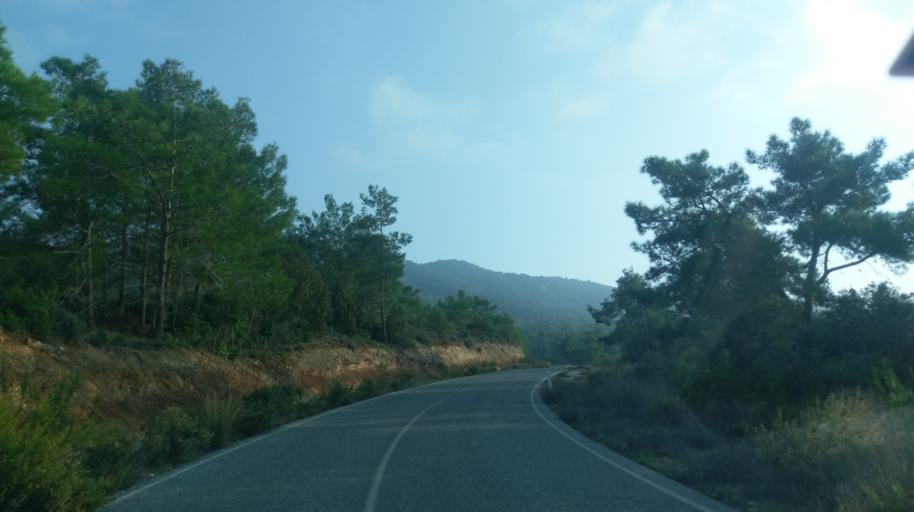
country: CY
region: Ammochostos
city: Trikomo
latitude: 35.4130
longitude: 33.9037
